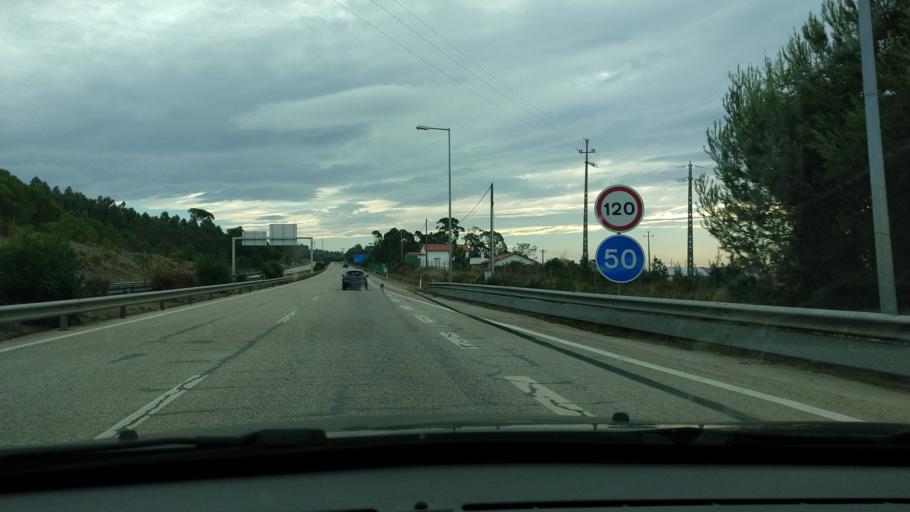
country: PT
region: Coimbra
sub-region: Figueira da Foz
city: Tavarede
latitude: 40.1496
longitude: -8.8286
